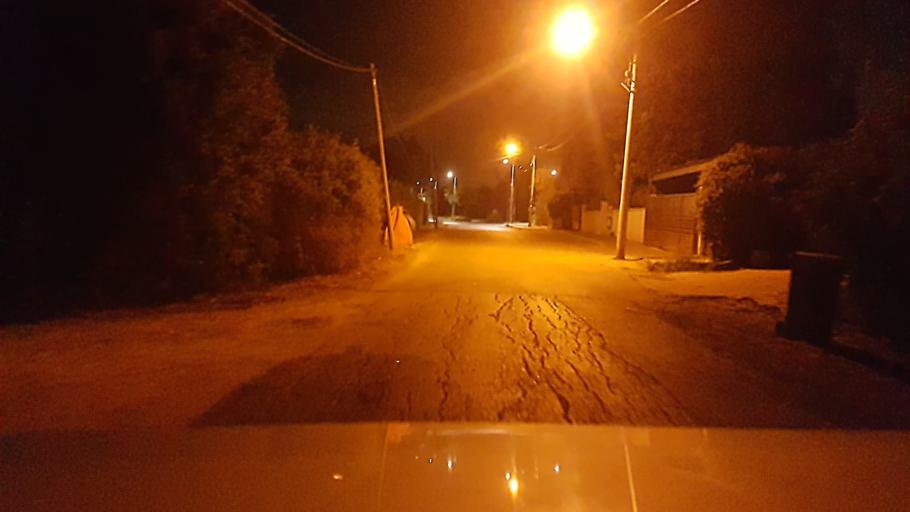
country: IL
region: Central District
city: Nehalim
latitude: 32.0779
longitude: 34.9301
